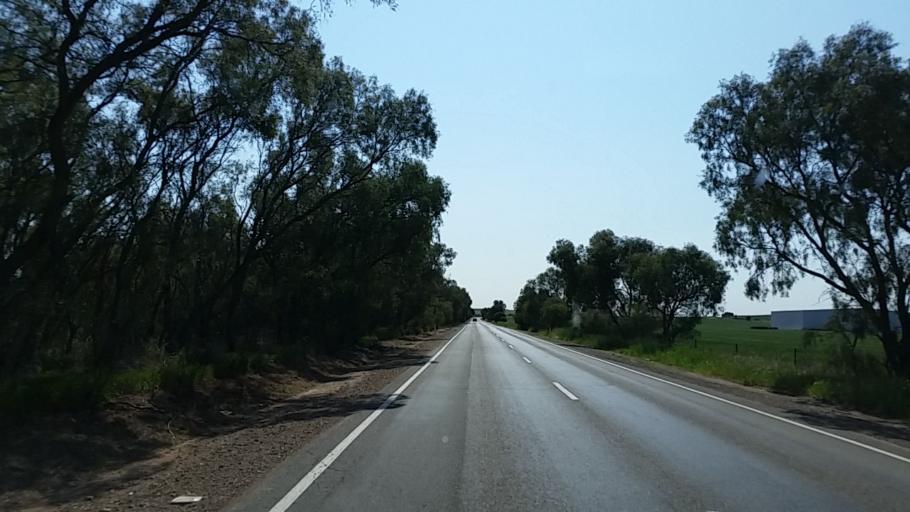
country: AU
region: South Australia
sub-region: Northern Areas
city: Jamestown
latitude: -33.2214
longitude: 138.4109
